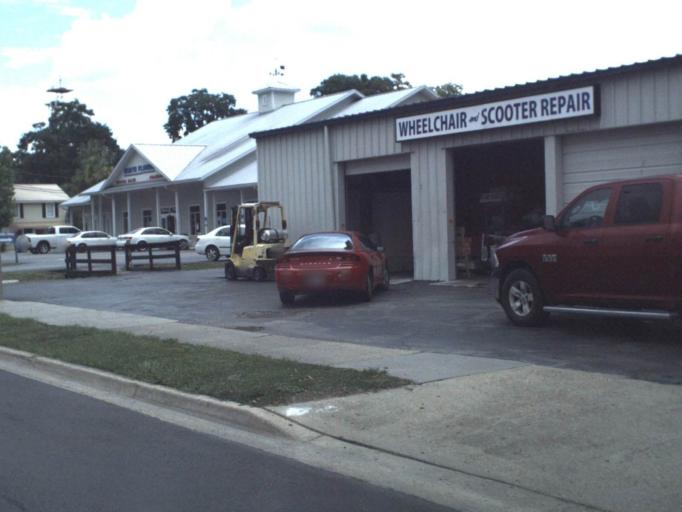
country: US
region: Florida
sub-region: Columbia County
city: Lake City
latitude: 30.1851
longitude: -82.6393
